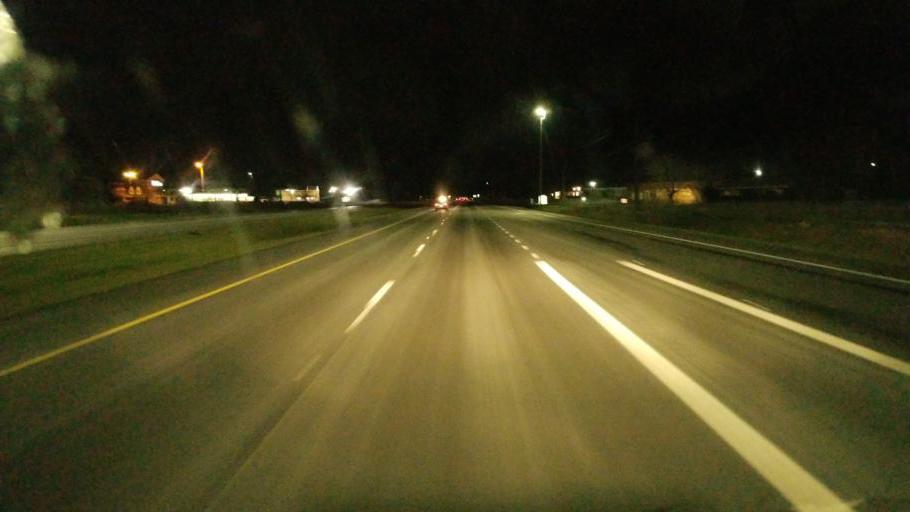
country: US
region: Ohio
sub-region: Licking County
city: Granville
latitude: 40.0549
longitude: -82.4788
